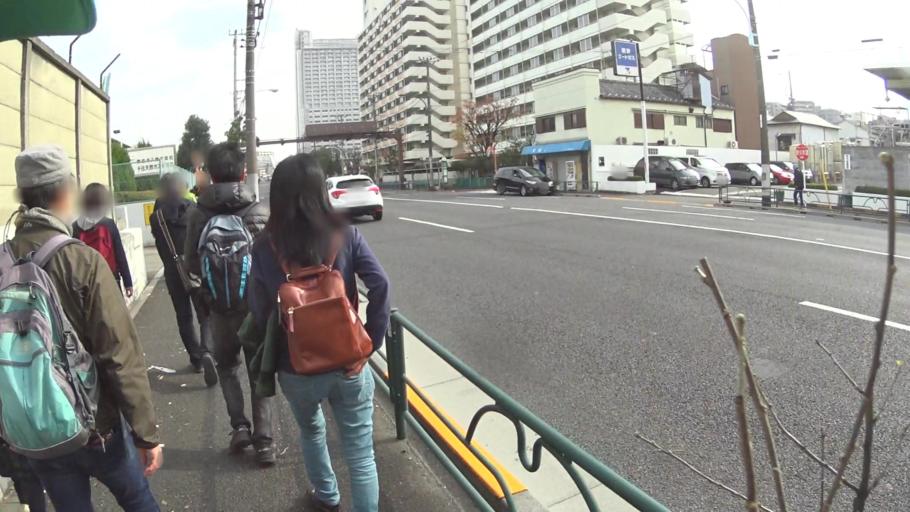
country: JP
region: Saitama
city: Soka
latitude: 35.7285
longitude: 139.8066
